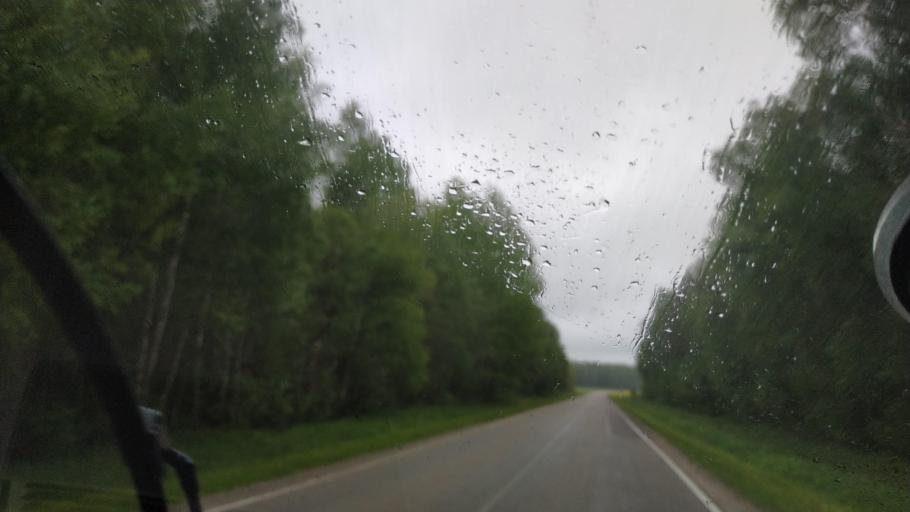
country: LT
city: Vabalninkas
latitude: 55.9984
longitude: 24.5953
